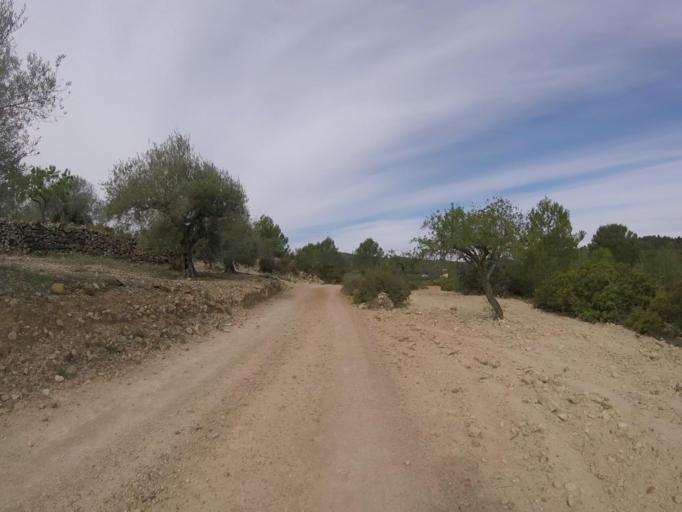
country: ES
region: Valencia
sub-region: Provincia de Castello
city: Cabanes
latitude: 40.1914
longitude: 0.1121
